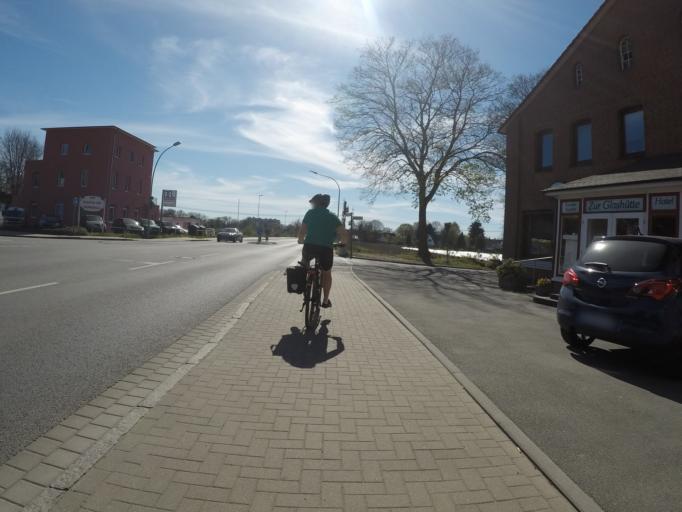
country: DE
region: Hamburg
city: Lemsahl-Mellingstedt
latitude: 53.6975
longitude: 10.0503
